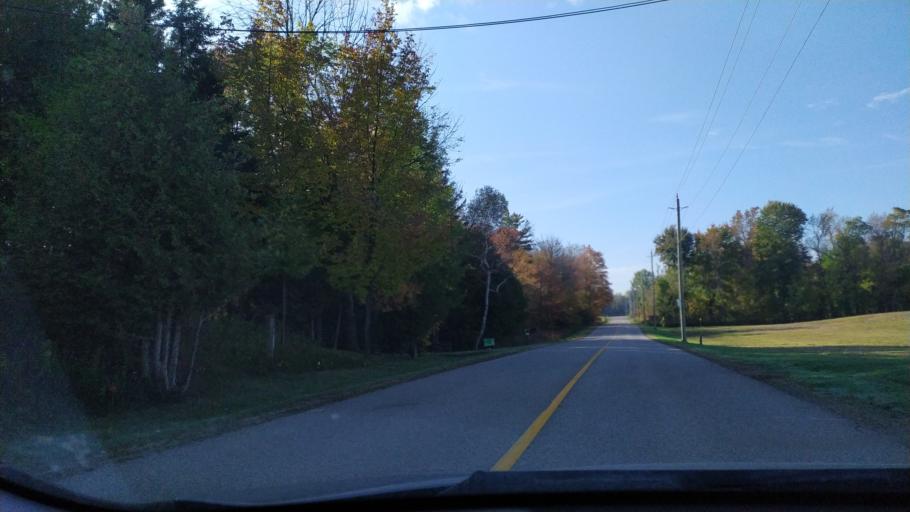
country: CA
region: Ontario
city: Waterloo
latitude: 43.5033
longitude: -80.6554
